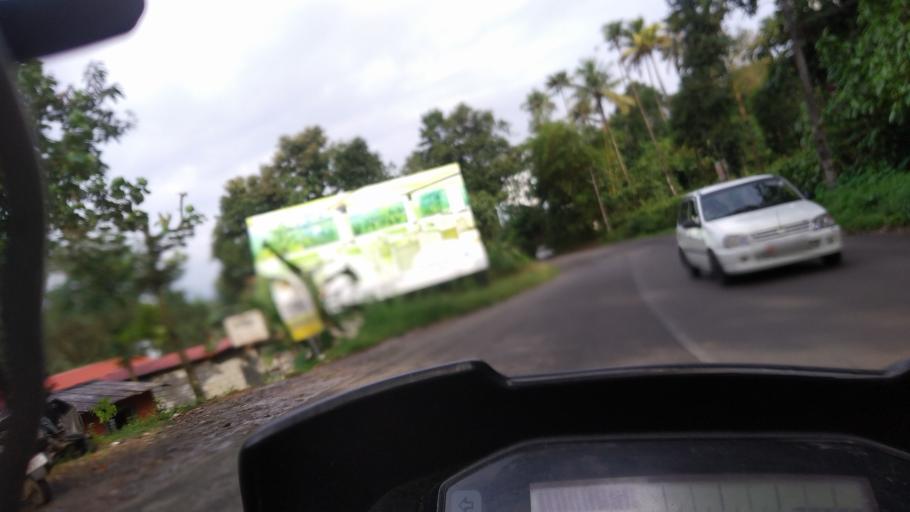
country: IN
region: Kerala
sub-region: Ernakulam
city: Kotamangalam
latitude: 10.0497
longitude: 76.7199
